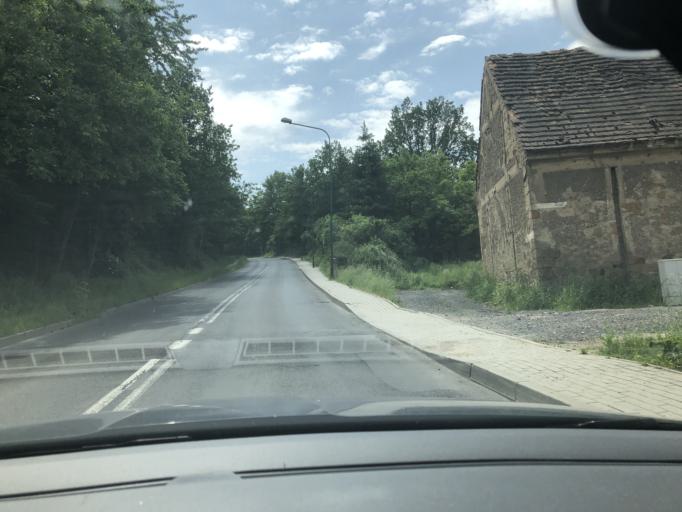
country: PL
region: Lower Silesian Voivodeship
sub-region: Powiat zlotoryjski
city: Zlotoryja
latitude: 51.1183
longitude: 15.9162
